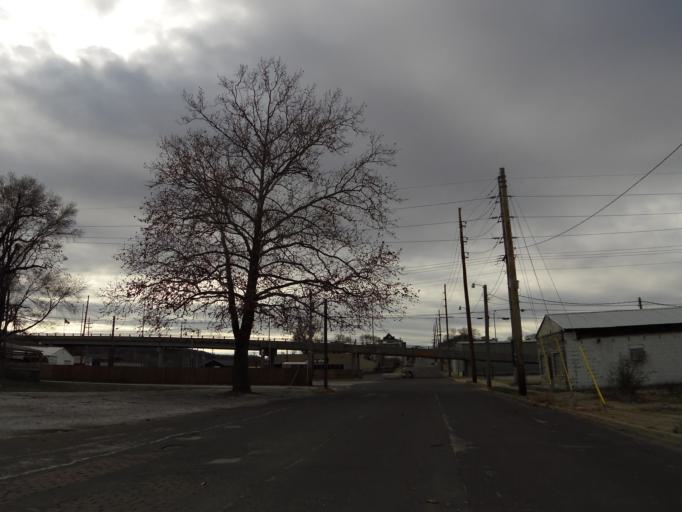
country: US
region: Missouri
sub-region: Marion County
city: Hannibal
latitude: 39.7083
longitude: -91.3549
